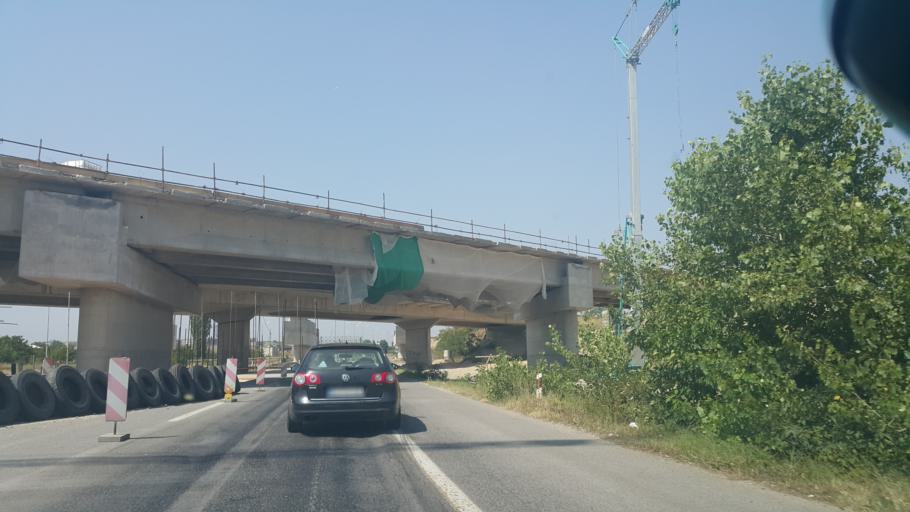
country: MK
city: Miladinovci
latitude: 41.9842
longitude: 21.6539
